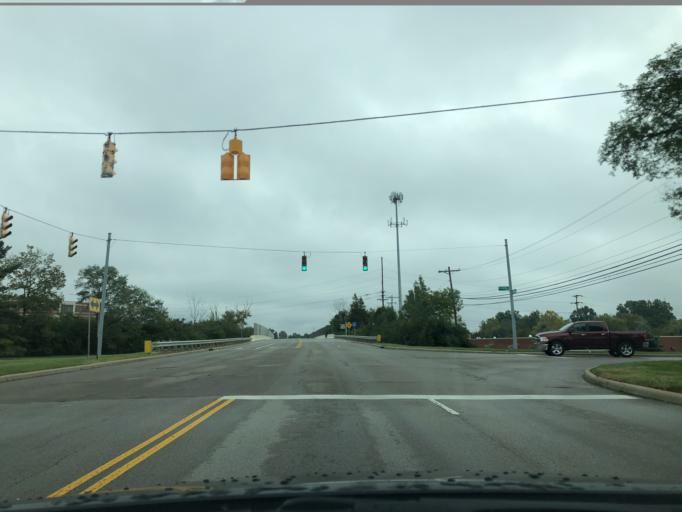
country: US
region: Ohio
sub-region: Hamilton County
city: Highpoint
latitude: 39.2825
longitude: -84.3688
